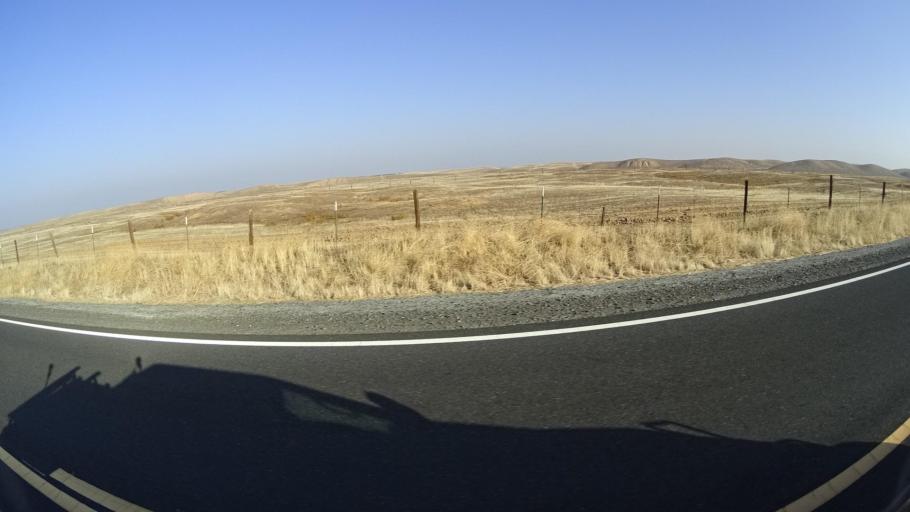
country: US
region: California
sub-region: Tulare County
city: Richgrove
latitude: 35.7619
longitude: -119.0420
